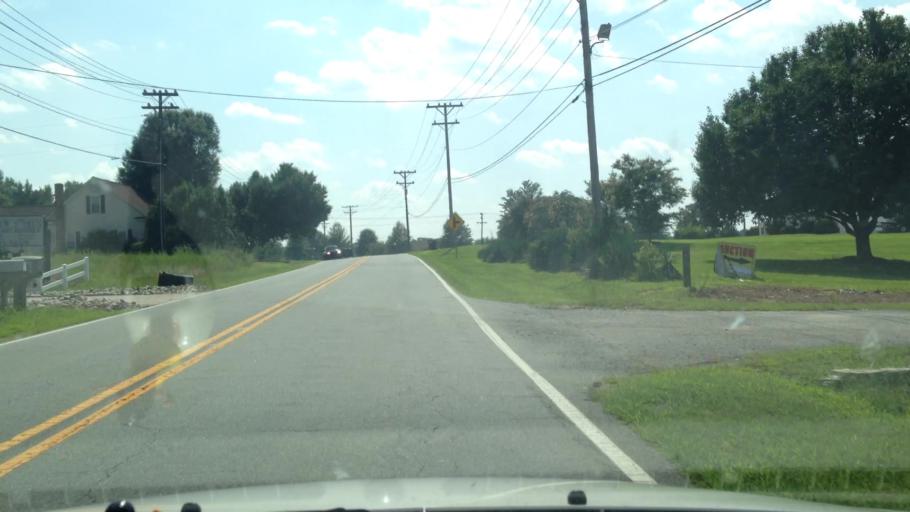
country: US
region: North Carolina
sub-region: Forsyth County
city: Kernersville
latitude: 36.1466
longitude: -80.0427
